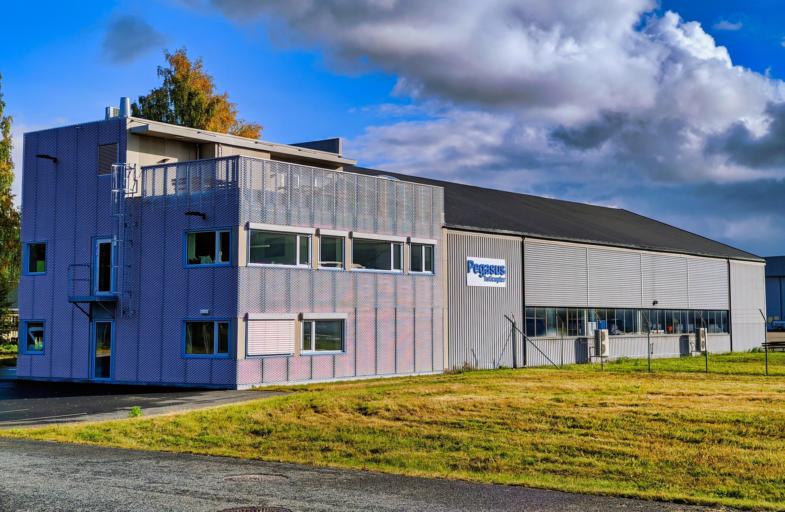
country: NO
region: Akershus
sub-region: Nannestad
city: Teigebyen
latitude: 60.2104
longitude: 11.0781
